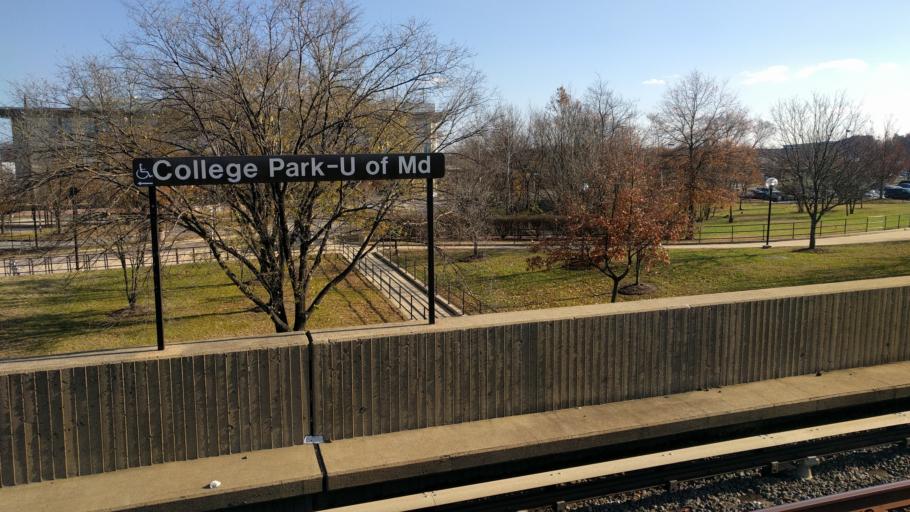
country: US
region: Maryland
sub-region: Prince George's County
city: College Park
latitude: 38.9778
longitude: -76.9285
